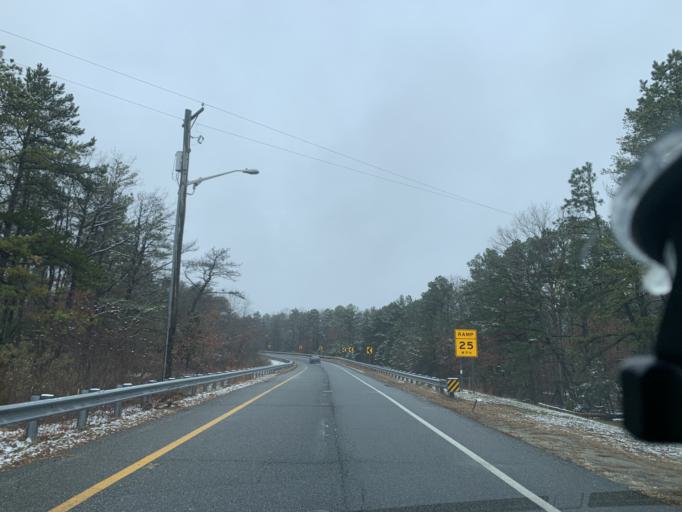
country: US
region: New Jersey
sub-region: Atlantic County
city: Pomona
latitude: 39.4478
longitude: -74.6211
